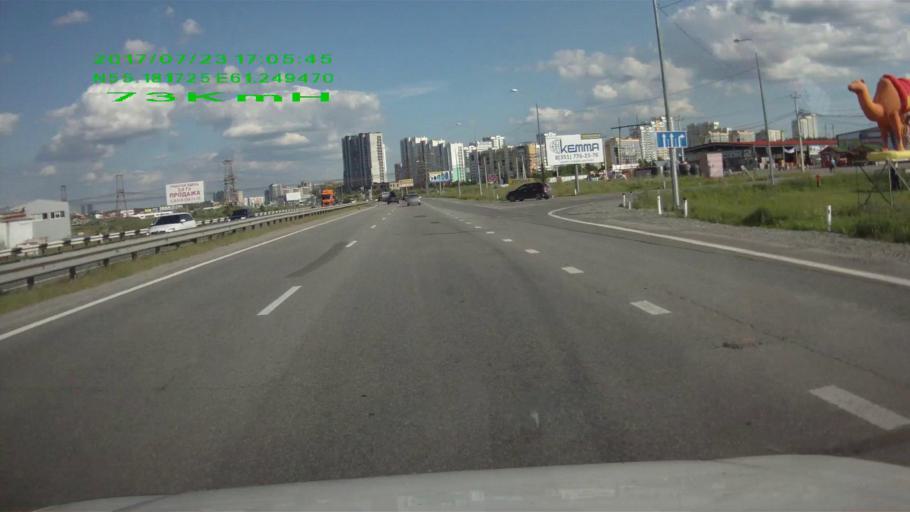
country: RU
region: Chelyabinsk
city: Roshchino
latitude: 55.1813
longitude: 61.2503
